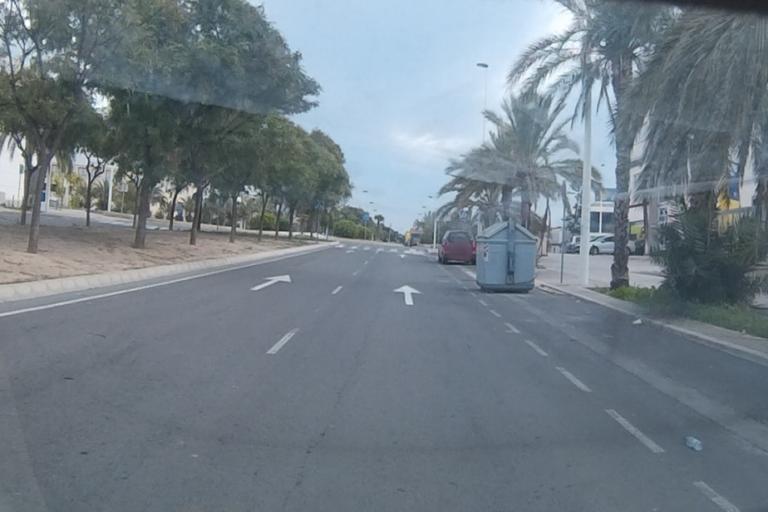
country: ES
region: Valencia
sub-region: Provincia de Alicante
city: Elche
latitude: 38.2945
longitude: -0.6137
